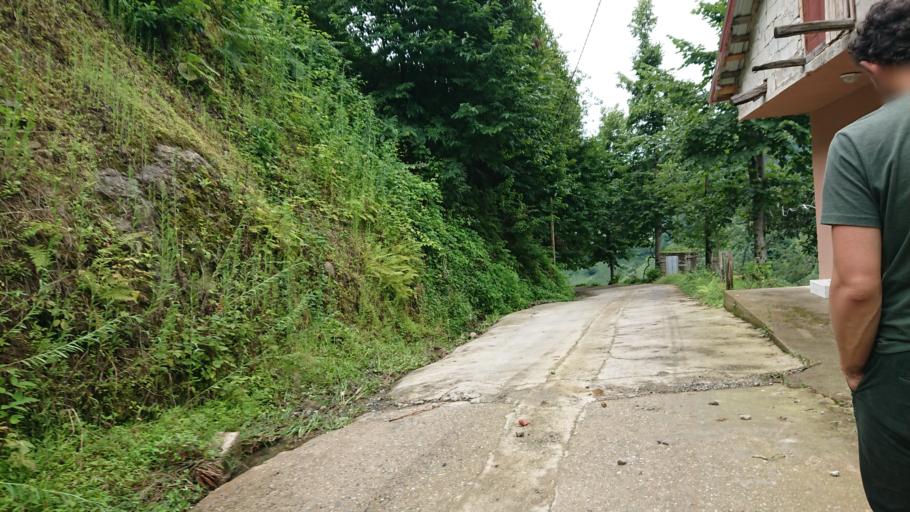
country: TR
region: Rize
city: Rize
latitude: 40.9752
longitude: 40.4854
